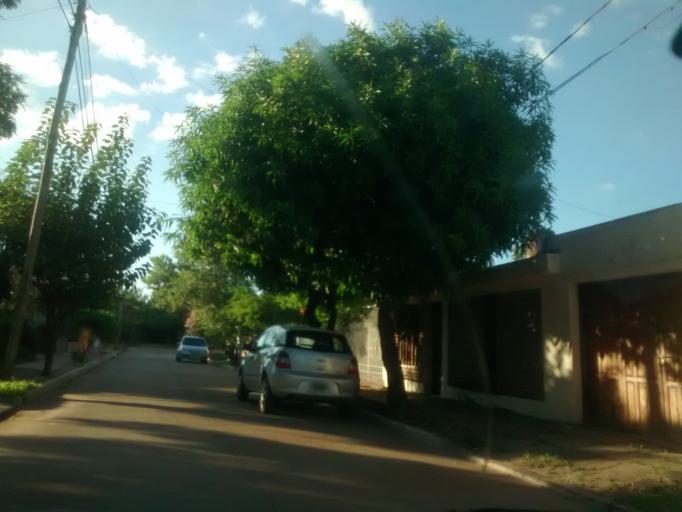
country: AR
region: Chaco
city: Fontana
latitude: -27.4412
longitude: -59.0153
